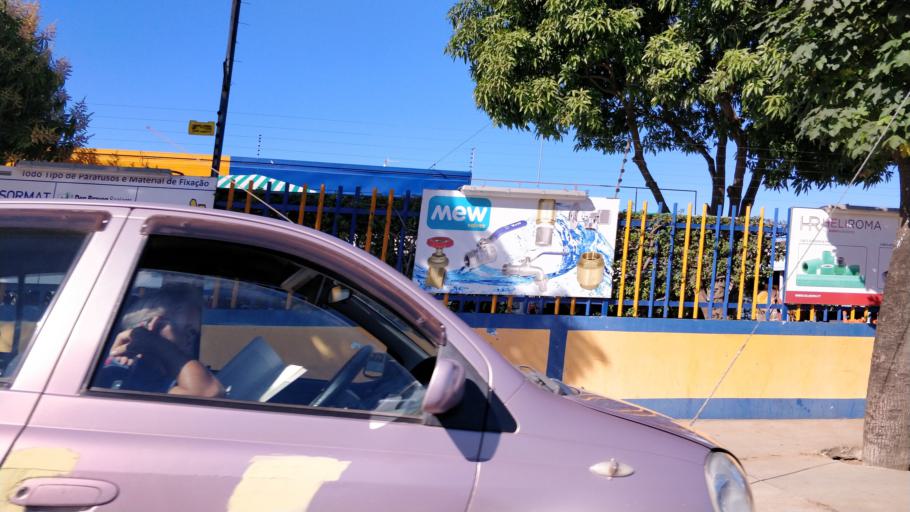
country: MZ
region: Maputo City
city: Maputo
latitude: -25.9283
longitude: 32.6000
